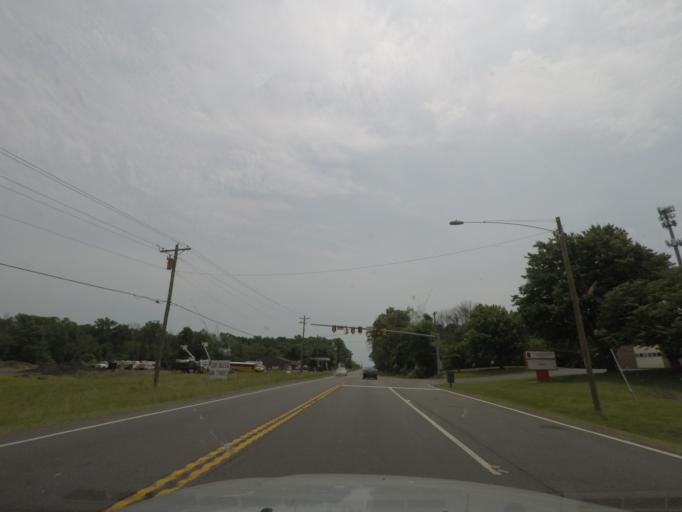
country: US
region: Virginia
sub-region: Prince William County
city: Bull Run Mountain Estates
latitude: 38.8813
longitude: -77.6336
